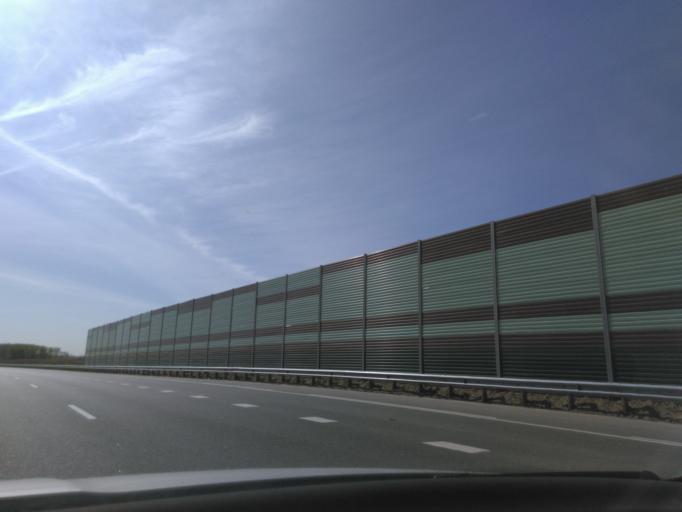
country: RU
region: Moskovskaya
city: Novopodrezkovo
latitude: 55.9557
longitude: 37.3699
